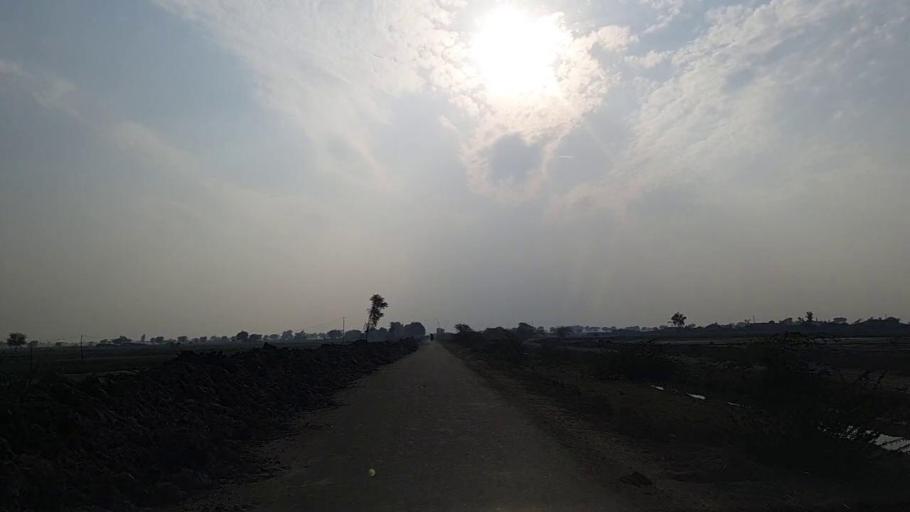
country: PK
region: Sindh
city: Jam Sahib
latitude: 26.3079
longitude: 68.5214
